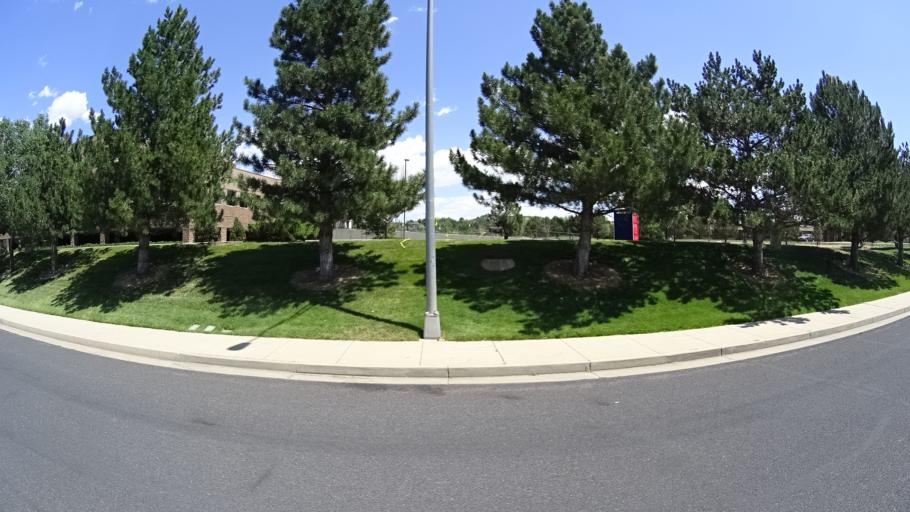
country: US
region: Colorado
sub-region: El Paso County
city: Colorado Springs
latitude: 38.8721
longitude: -104.7947
